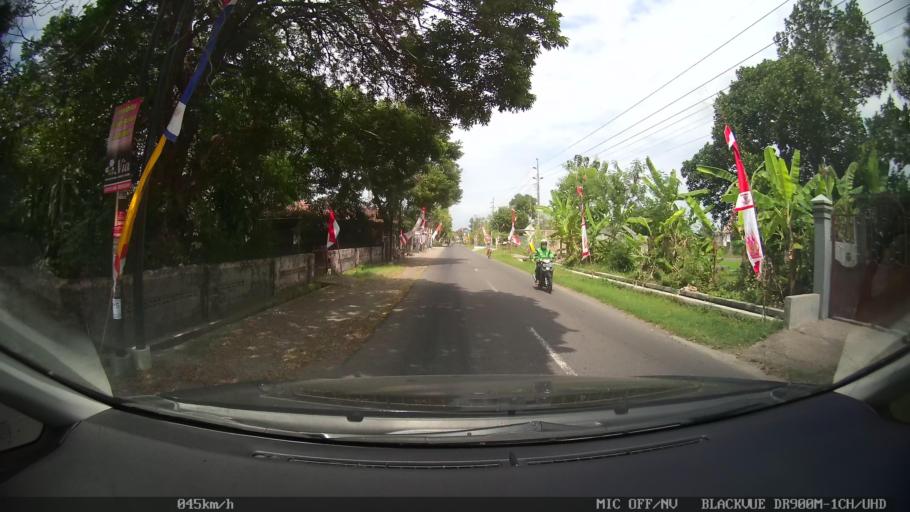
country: ID
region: Daerah Istimewa Yogyakarta
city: Depok
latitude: -7.8024
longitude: 110.4536
